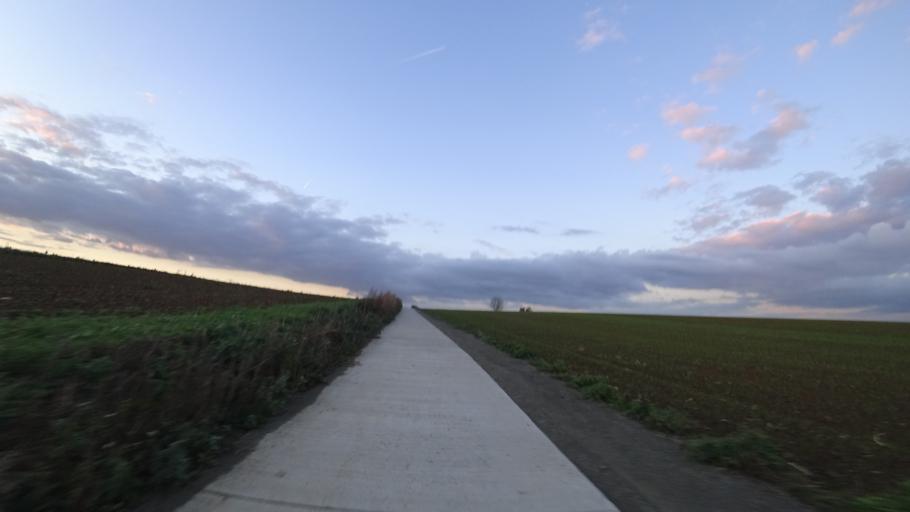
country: BE
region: Wallonia
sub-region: Province de Namur
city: Gembloux
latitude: 50.5634
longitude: 4.7152
